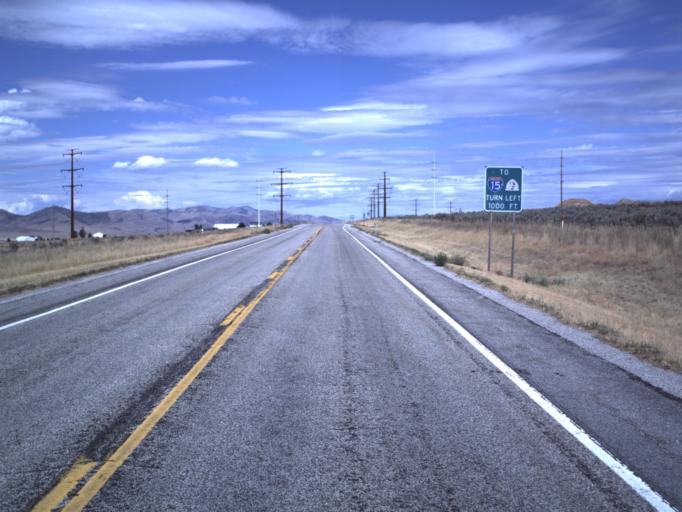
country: US
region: Utah
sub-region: Box Elder County
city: Garland
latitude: 41.8843
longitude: -112.1585
